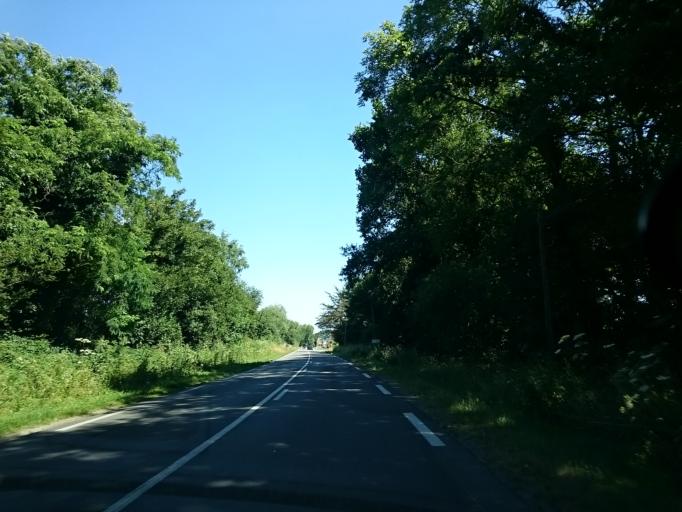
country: FR
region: Brittany
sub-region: Departement d'Ille-et-Vilaine
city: Saint-Pere
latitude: 48.5678
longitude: -1.9196
